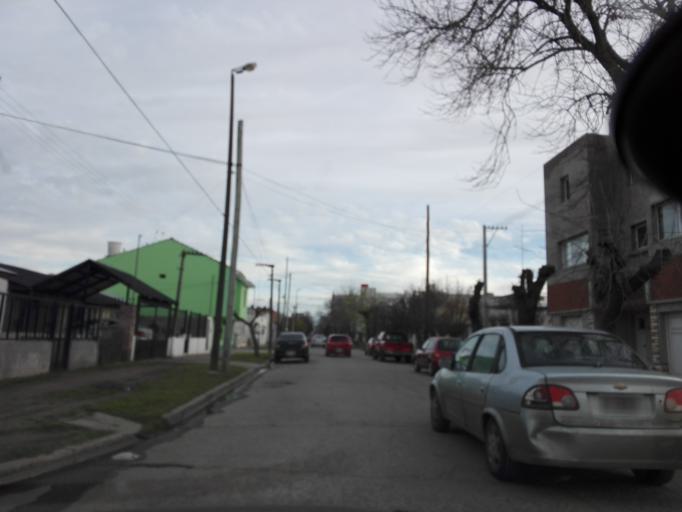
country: AR
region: Buenos Aires
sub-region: Partido de Balcarce
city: Balcarce
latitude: -37.8449
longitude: -58.2496
